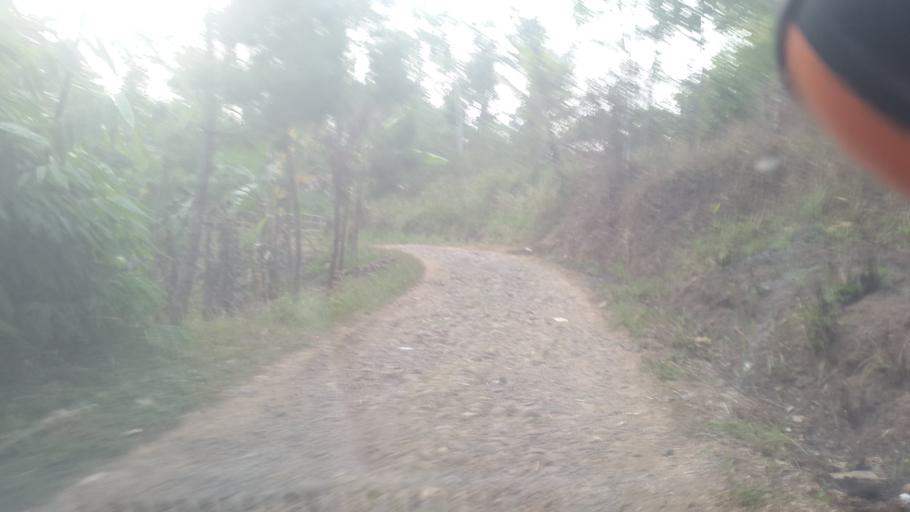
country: ID
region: West Java
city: Sukamaju
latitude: -7.0033
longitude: 106.8845
